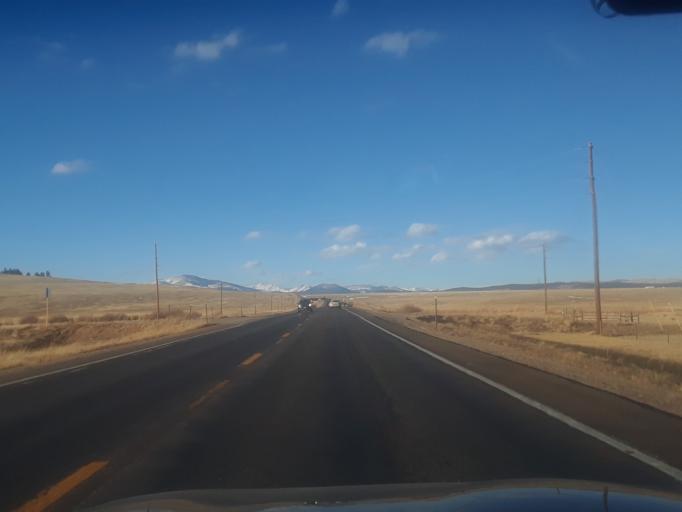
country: US
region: Colorado
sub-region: Park County
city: Fairplay
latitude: 39.0699
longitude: -105.9744
